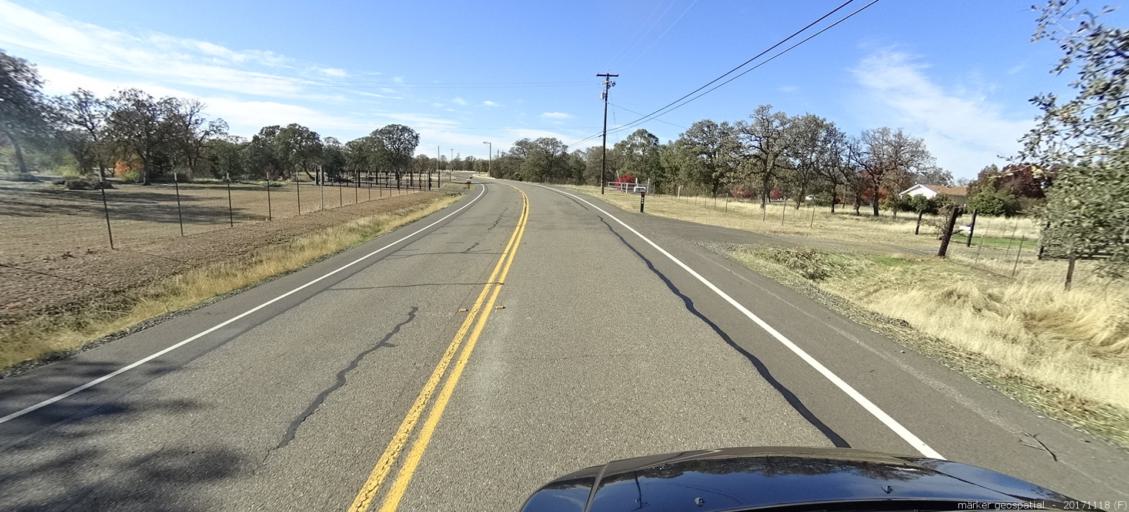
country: US
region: California
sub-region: Shasta County
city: Anderson
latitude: 40.4414
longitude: -122.3438
